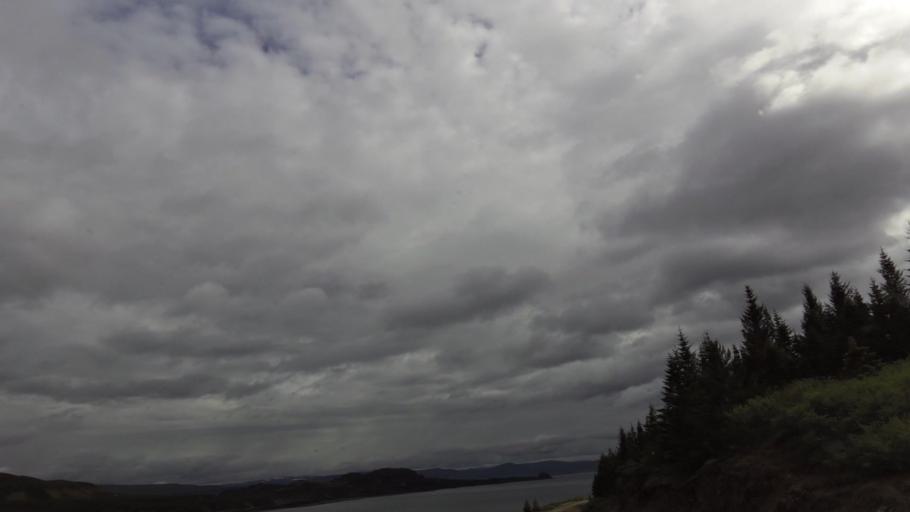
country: IS
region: West
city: Stykkisholmur
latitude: 65.5178
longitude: -22.1135
